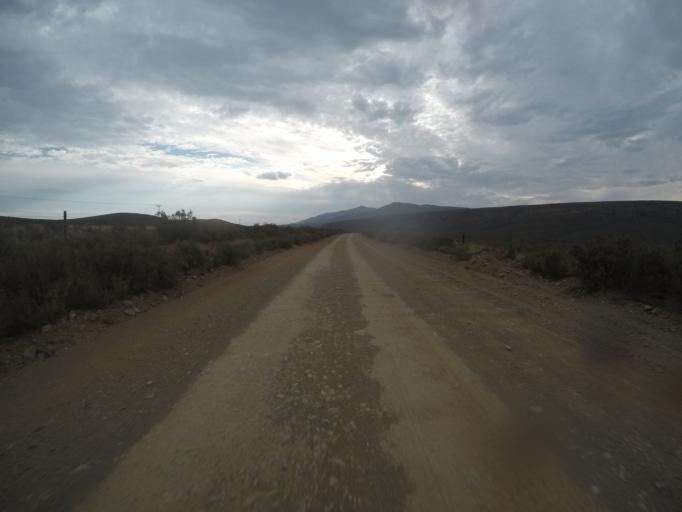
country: ZA
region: Eastern Cape
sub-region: Cacadu District Municipality
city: Willowmore
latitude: -33.4906
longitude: 23.5653
